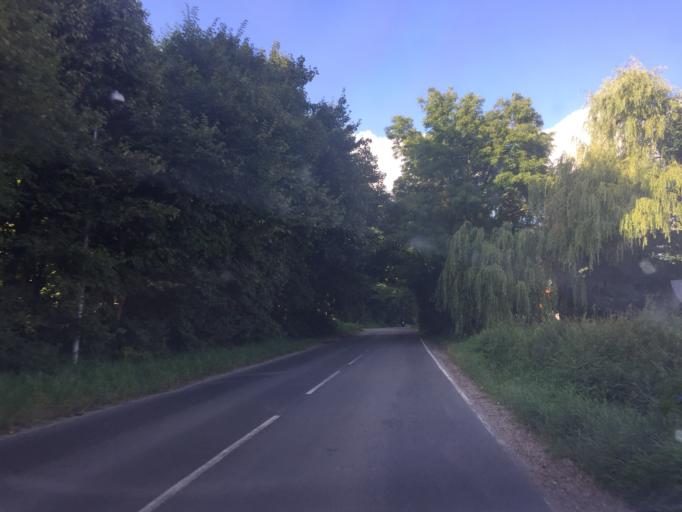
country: DK
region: Capital Region
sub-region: Hoje-Taastrup Kommune
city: Taastrup
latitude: 55.6916
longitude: 12.2458
